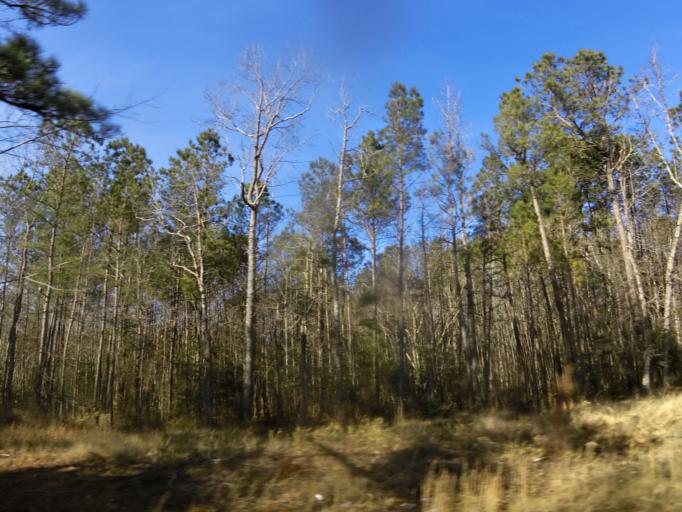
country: US
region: Virginia
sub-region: Isle of Wight County
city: Isle of Wight
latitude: 36.8912
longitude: -76.7281
